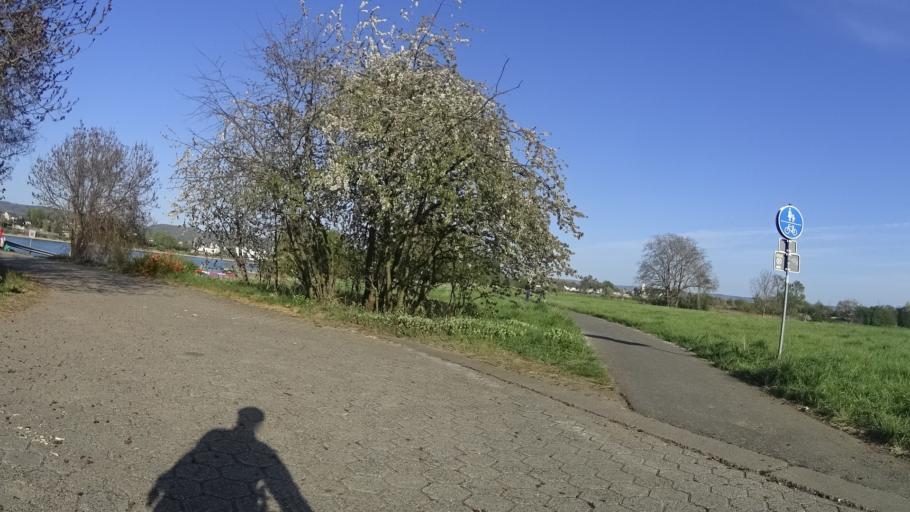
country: DE
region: Rheinland-Pfalz
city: Urmitz
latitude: 50.4199
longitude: 7.5306
